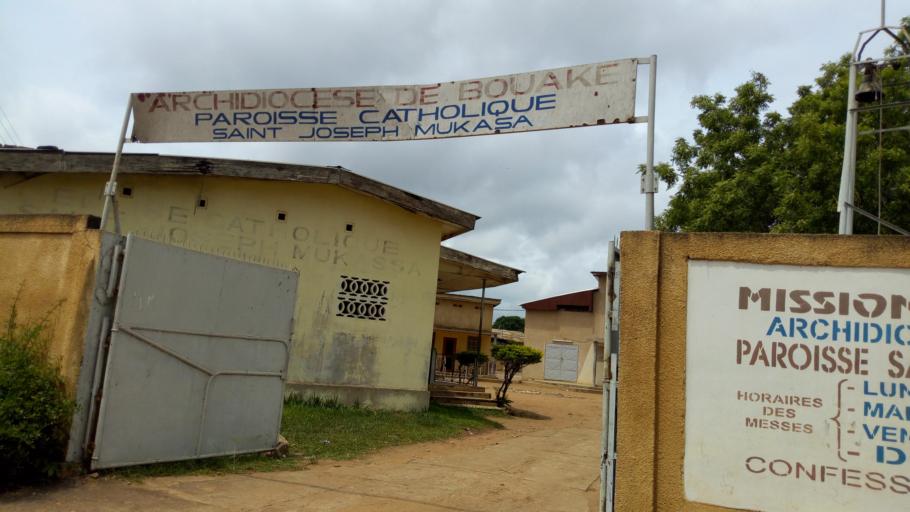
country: CI
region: Vallee du Bandama
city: Bouake
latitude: 7.6907
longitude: -5.0109
